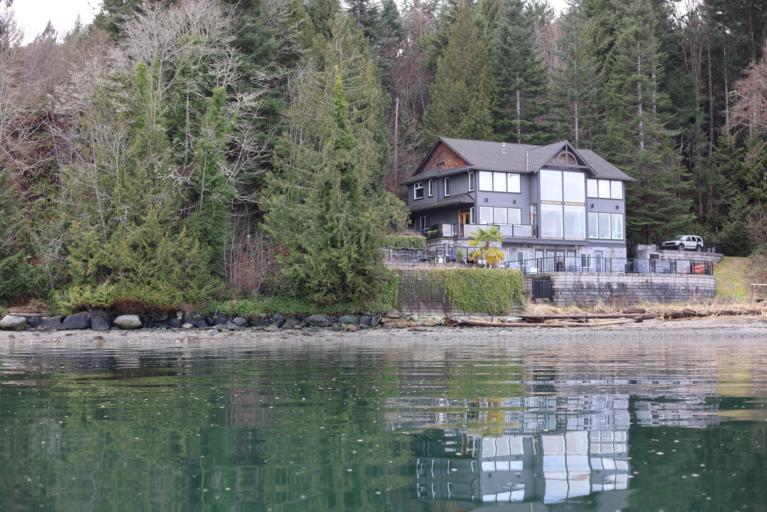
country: CA
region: British Columbia
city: Duncan
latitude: 48.7260
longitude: -123.5702
